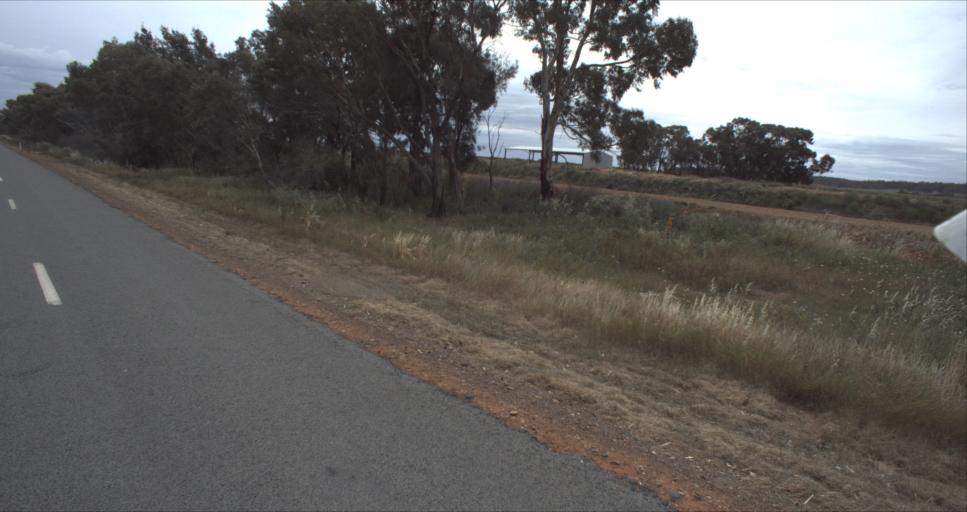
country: AU
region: New South Wales
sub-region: Leeton
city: Leeton
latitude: -34.4457
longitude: 146.3806
